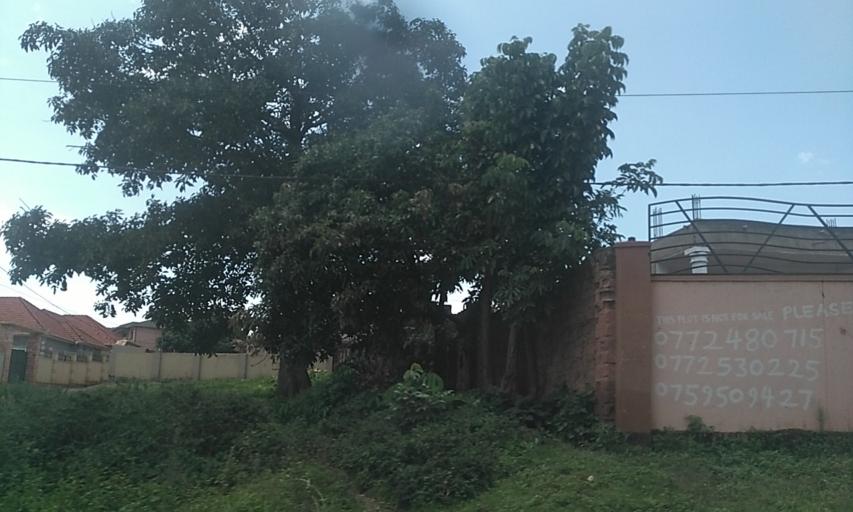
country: UG
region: Central Region
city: Kampala Central Division
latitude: 0.3877
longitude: 32.5930
